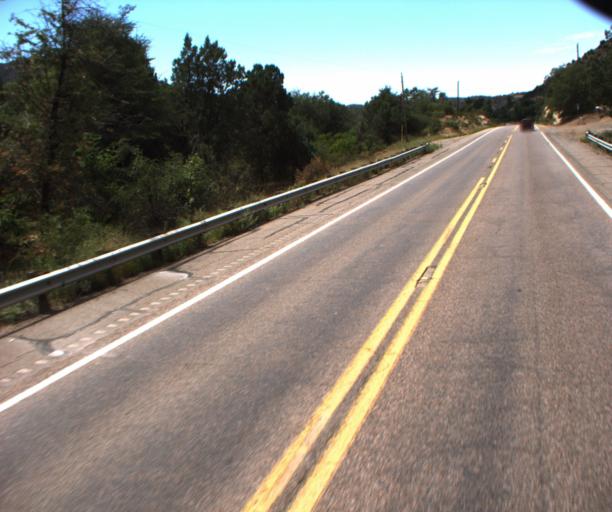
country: US
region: Arizona
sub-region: Pinal County
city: Superior
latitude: 33.3482
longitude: -110.9929
